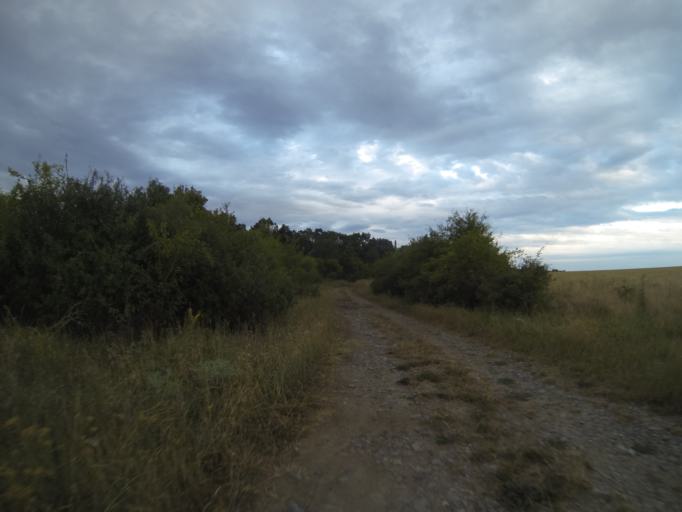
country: RO
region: Dolj
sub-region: Comuna Almaju
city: Almaju
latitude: 44.4740
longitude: 23.7036
